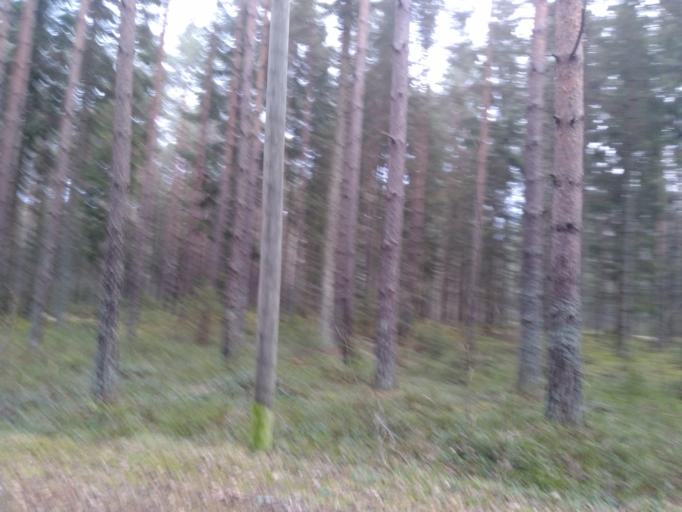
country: SE
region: Vaestra Goetaland
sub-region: Lidkopings Kommun
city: Lidkoping
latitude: 58.4858
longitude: 13.1624
